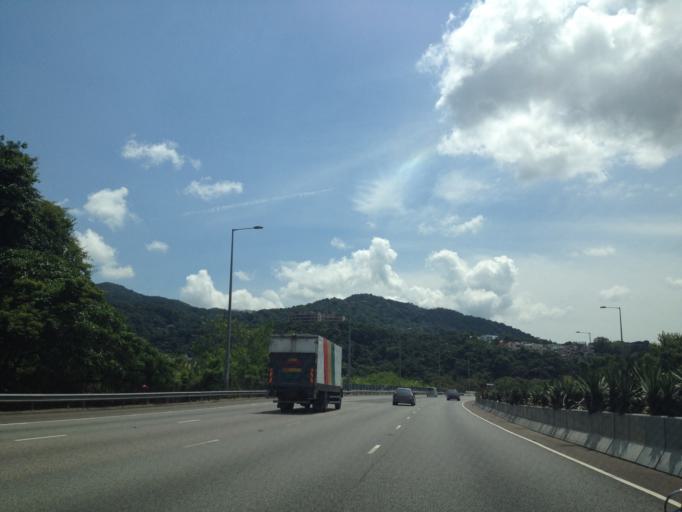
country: HK
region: Tai Po
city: Tai Po
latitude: 22.4394
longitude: 114.1911
